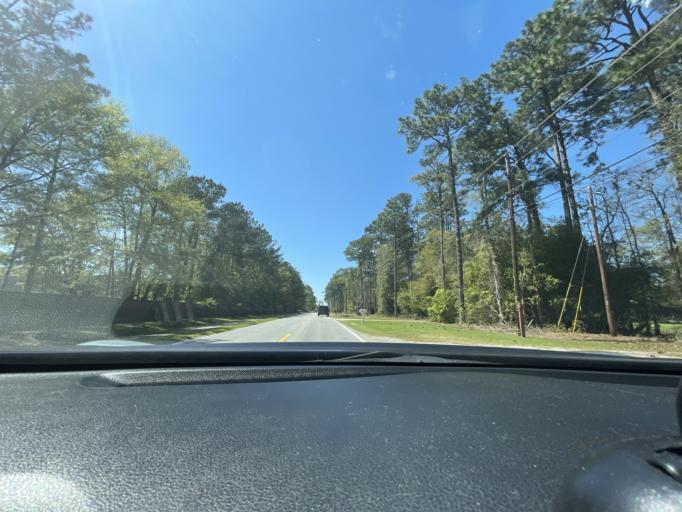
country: US
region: Georgia
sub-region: Chatham County
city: Pooler
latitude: 32.0912
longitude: -81.2512
